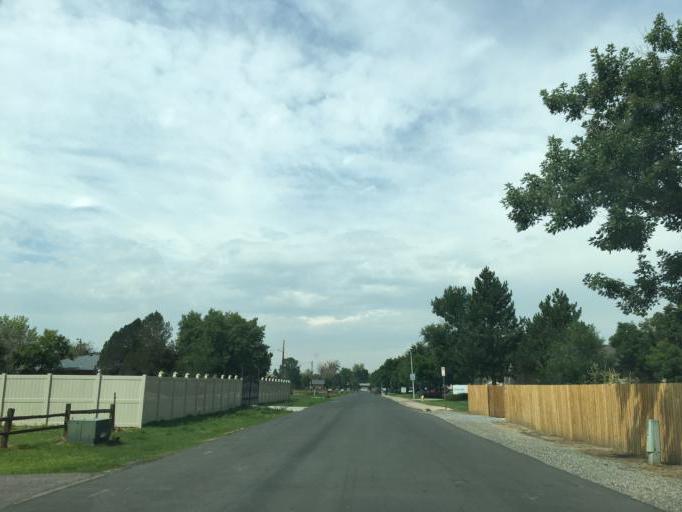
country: US
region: Colorado
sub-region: Adams County
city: Aurora
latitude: 39.7366
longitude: -104.8011
